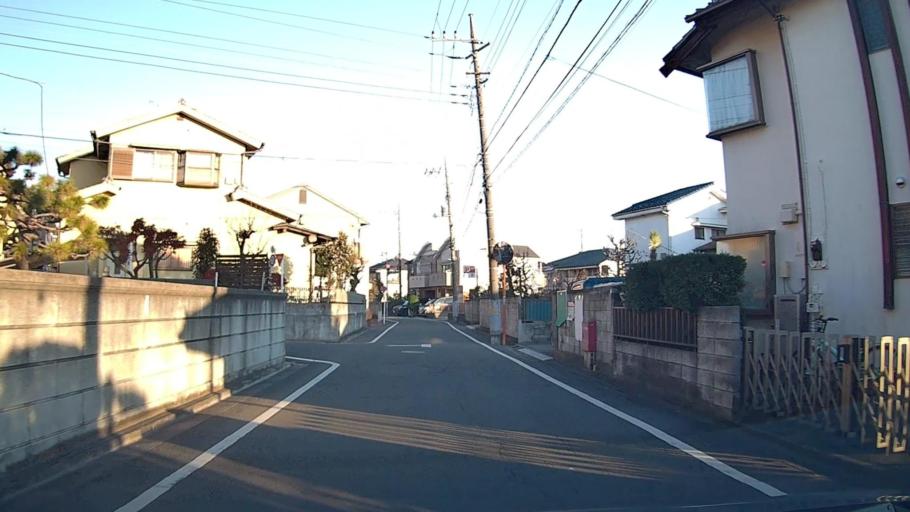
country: JP
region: Saitama
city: Wako
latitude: 35.7643
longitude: 139.6405
